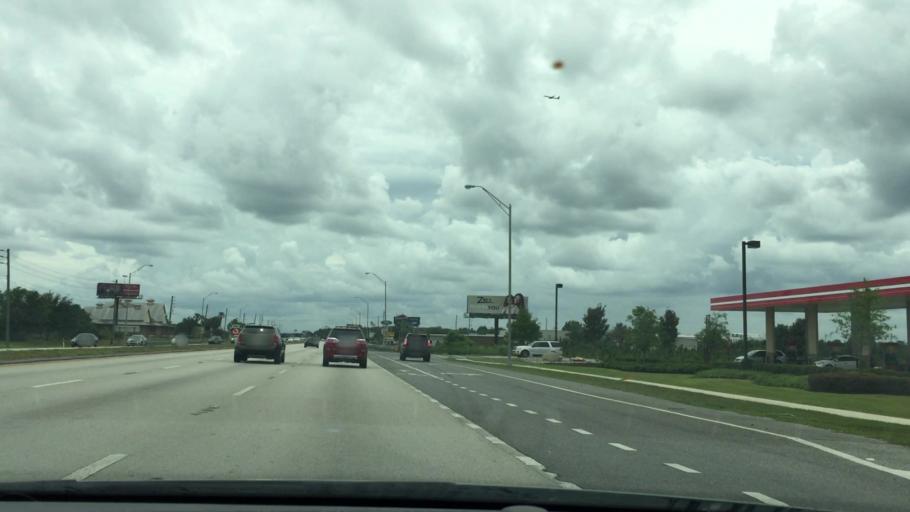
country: US
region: Florida
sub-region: Osceola County
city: Kissimmee
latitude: 28.3014
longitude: -81.3760
